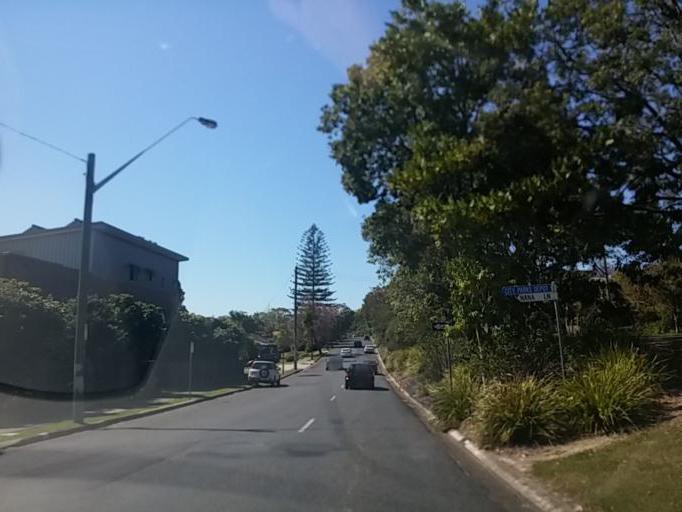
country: AU
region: New South Wales
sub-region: Coffs Harbour
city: Coffs Harbour
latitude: -30.3036
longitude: 153.1248
